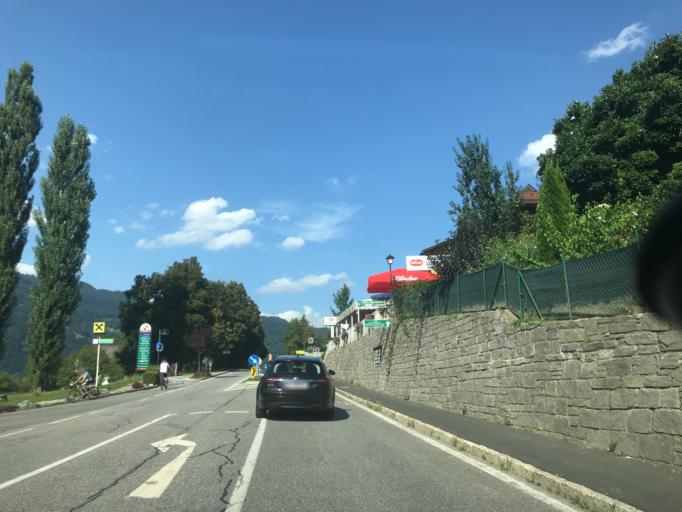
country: AT
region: Carinthia
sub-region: Politischer Bezirk Feldkirchen
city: Ossiach
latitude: 46.6749
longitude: 13.9845
